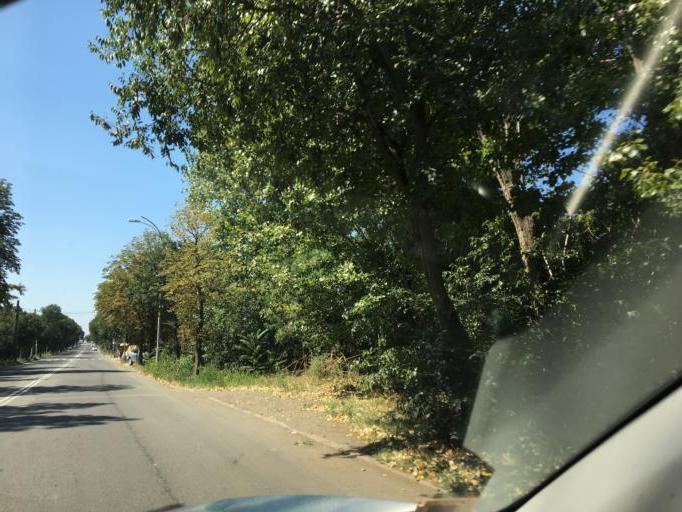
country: BG
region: Burgas
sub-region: Obshtina Kameno
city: Kameno
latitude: 42.6089
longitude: 27.3905
